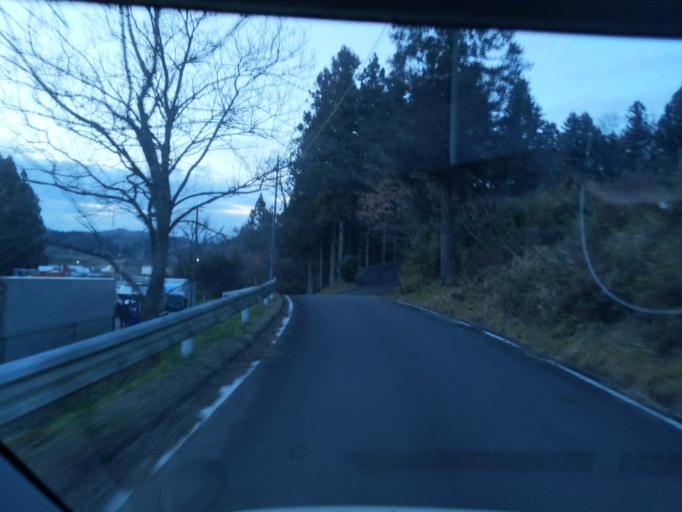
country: JP
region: Iwate
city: Ichinoseki
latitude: 38.8327
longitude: 141.0879
